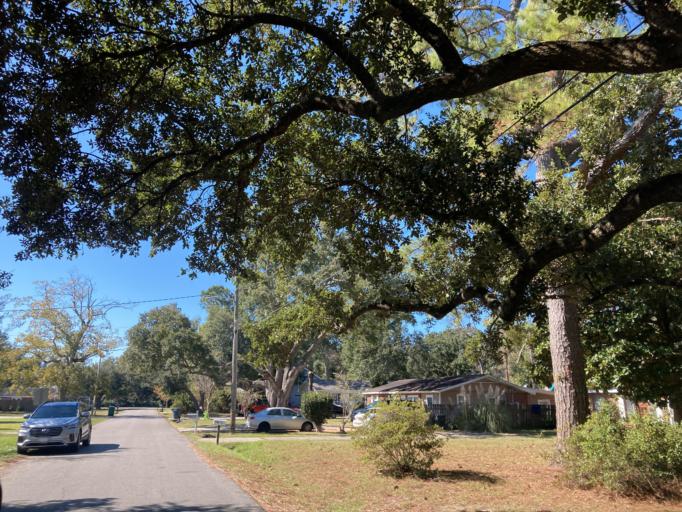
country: US
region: Mississippi
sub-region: Jackson County
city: Ocean Springs
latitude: 30.4092
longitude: -88.8147
